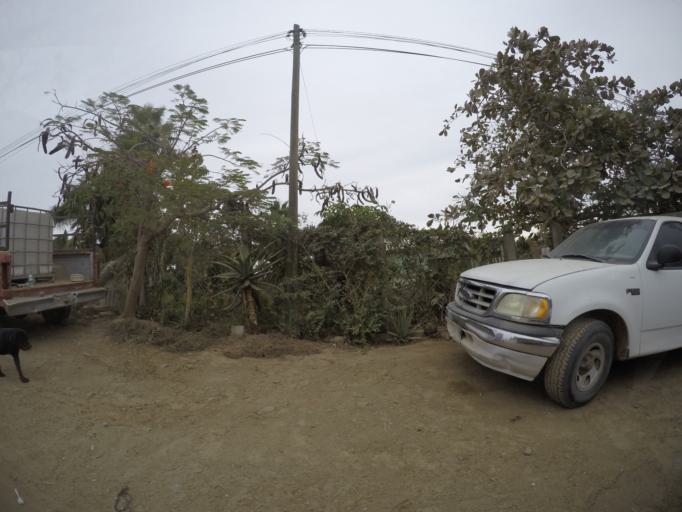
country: MX
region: Baja California Sur
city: Todos Santos
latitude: 23.4404
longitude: -110.2288
